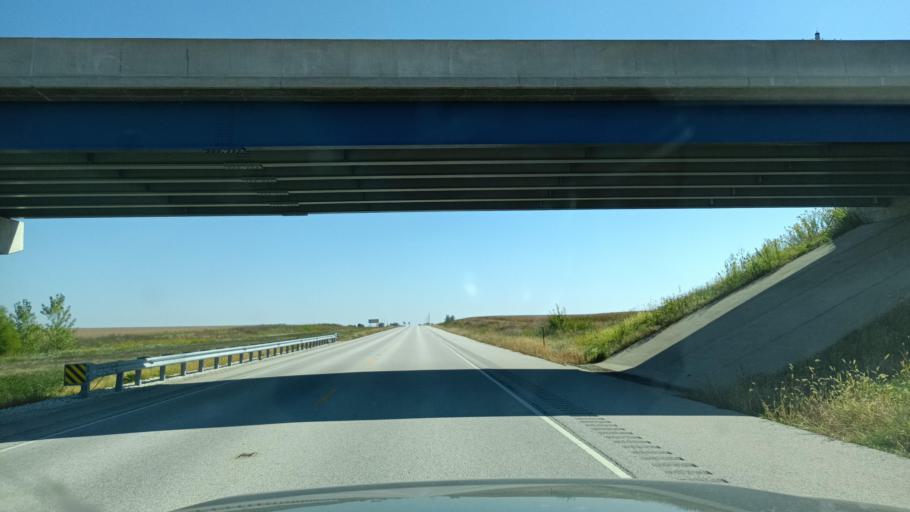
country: US
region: Illinois
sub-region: McDonough County
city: Macomb
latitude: 40.5034
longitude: -90.6950
